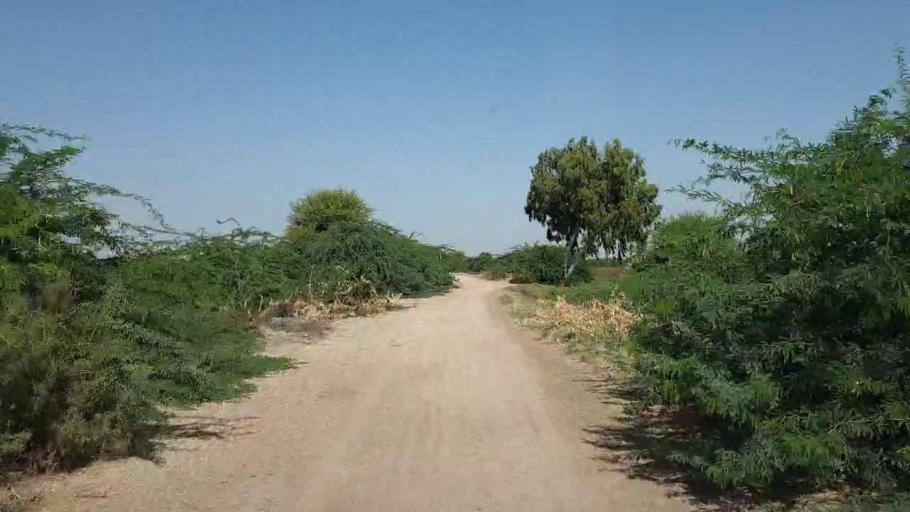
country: PK
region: Sindh
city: Tando Bago
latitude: 24.7366
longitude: 69.0427
